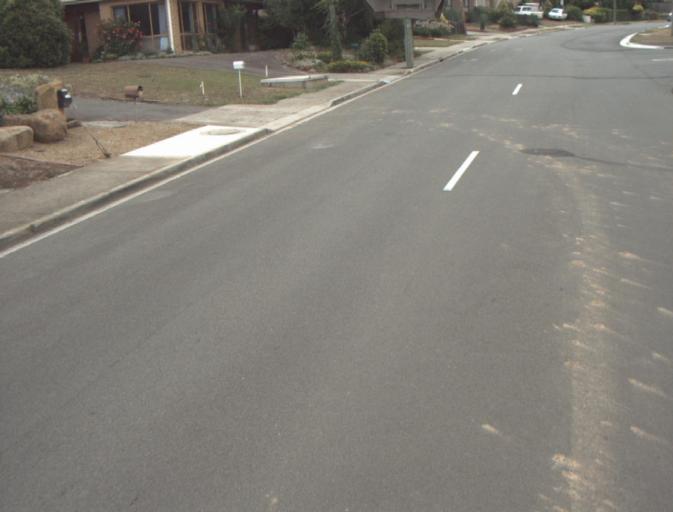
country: AU
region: Tasmania
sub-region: Launceston
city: Launceston
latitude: -41.4305
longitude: 147.1118
